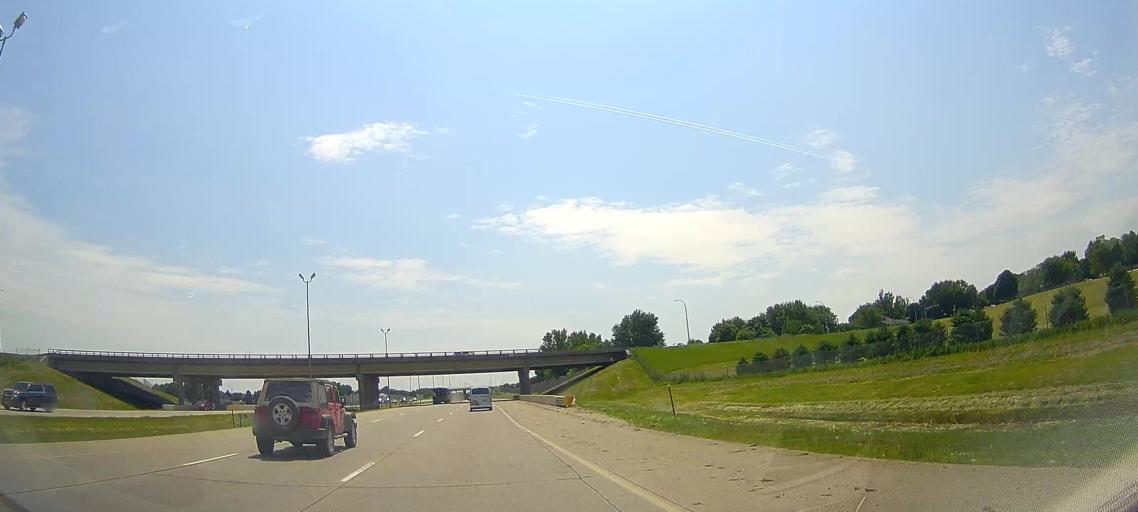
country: US
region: South Dakota
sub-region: Lincoln County
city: Tea
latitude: 43.5082
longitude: -96.7833
